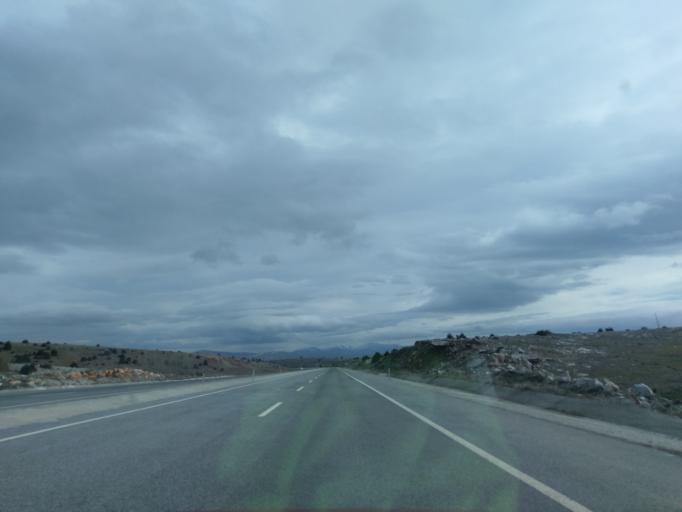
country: TR
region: Kuetahya
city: Aslanapa
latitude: 39.2333
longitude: 29.7797
